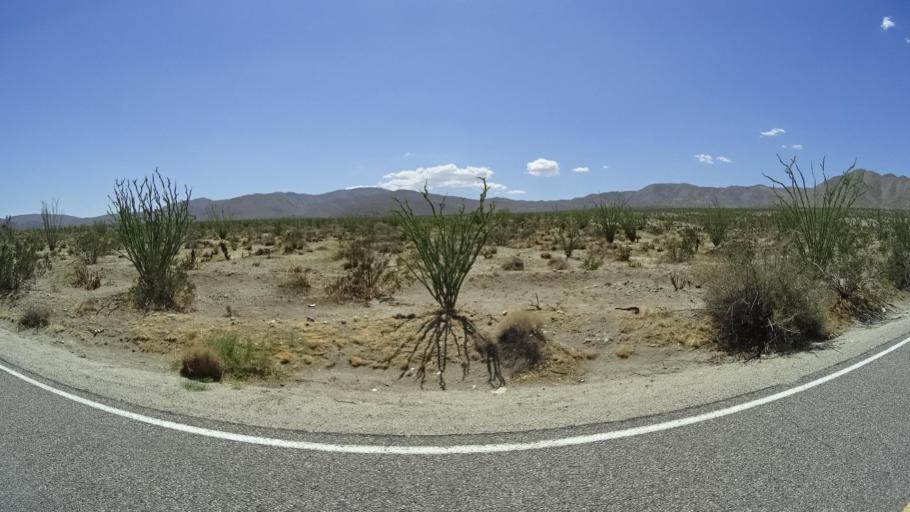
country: US
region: California
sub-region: San Diego County
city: Borrego Springs
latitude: 33.1342
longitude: -116.3430
